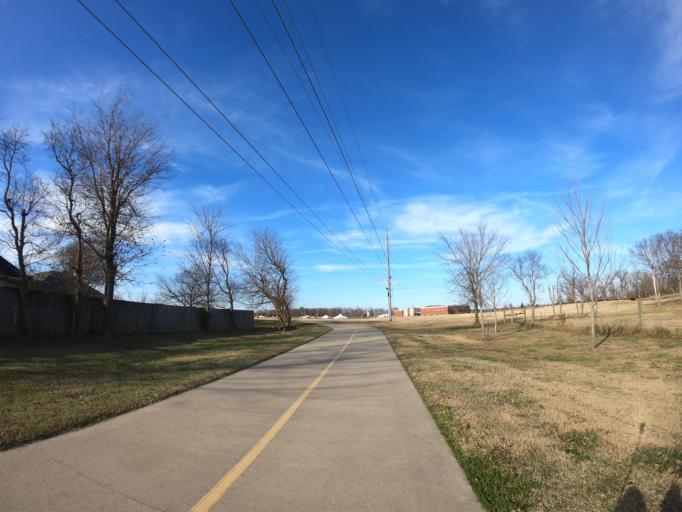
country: US
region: Arkansas
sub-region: Benton County
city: Lowell
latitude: 36.2761
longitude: -94.1675
